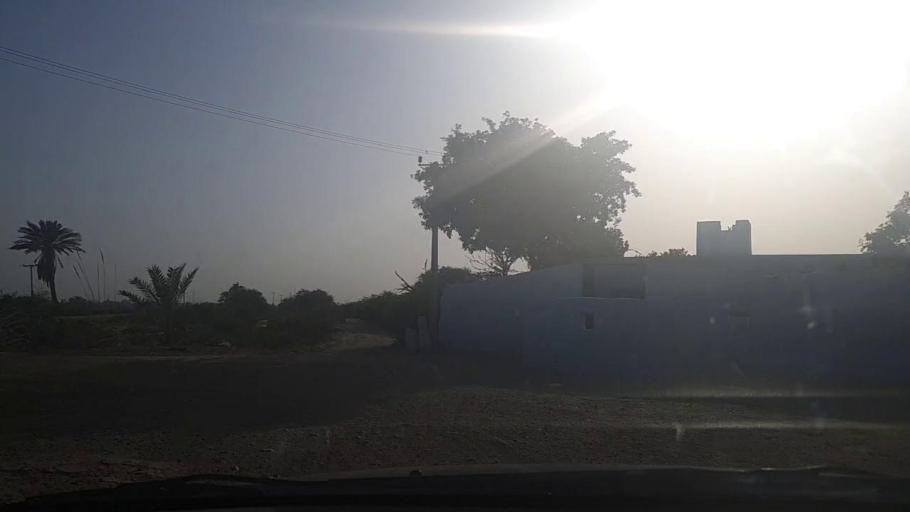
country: PK
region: Sindh
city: Keti Bandar
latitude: 24.2914
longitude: 67.6087
